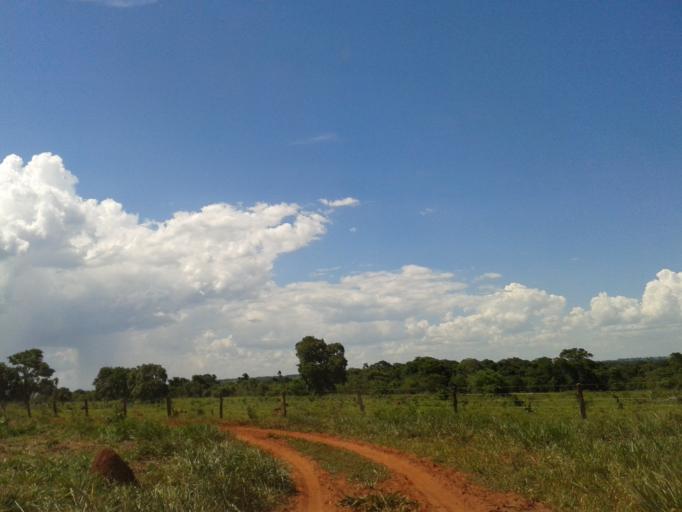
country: BR
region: Minas Gerais
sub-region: Santa Vitoria
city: Santa Vitoria
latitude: -19.1389
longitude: -50.5508
